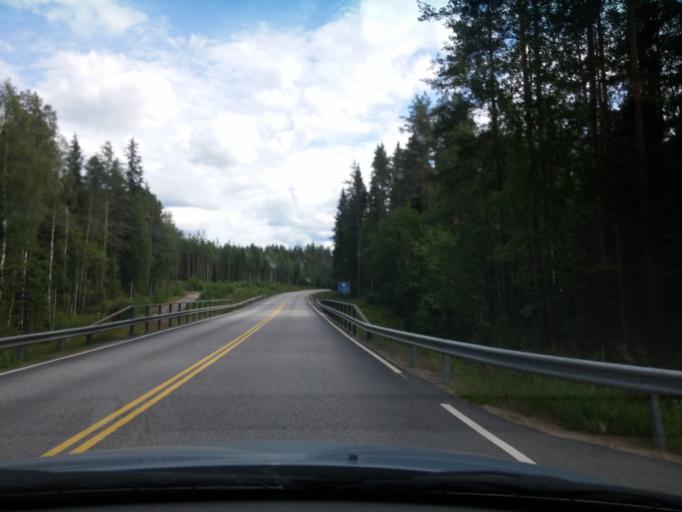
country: FI
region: Central Finland
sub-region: Keuruu
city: Multia
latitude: 62.4897
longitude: 24.6926
